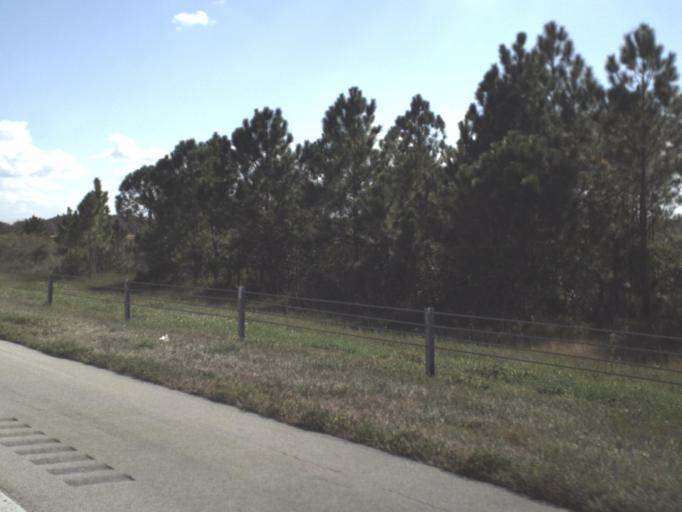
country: US
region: Florida
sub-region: Osceola County
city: Saint Cloud
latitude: 27.9487
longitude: -81.0861
